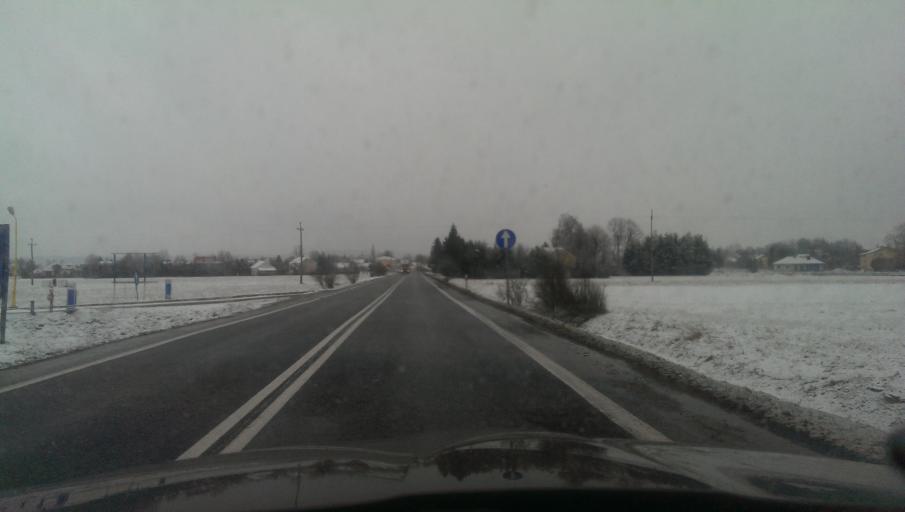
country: PL
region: Subcarpathian Voivodeship
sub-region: Powiat sanocki
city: Zarszyn
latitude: 49.5819
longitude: 21.9996
